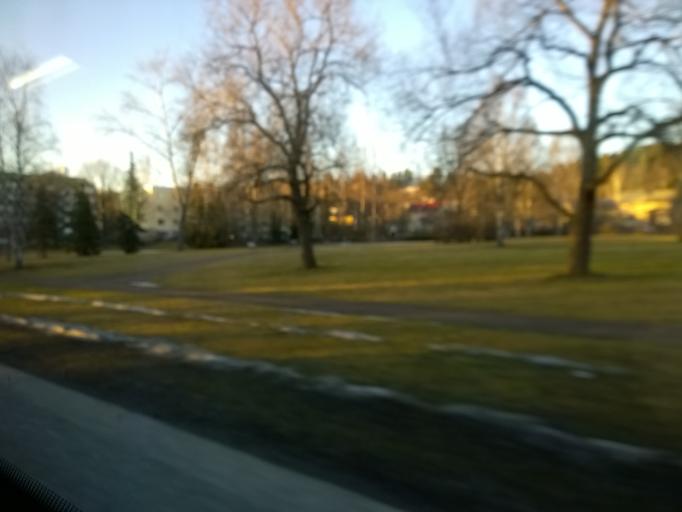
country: FI
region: Pirkanmaa
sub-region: Tampere
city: Tampere
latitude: 61.4884
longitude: 23.8026
